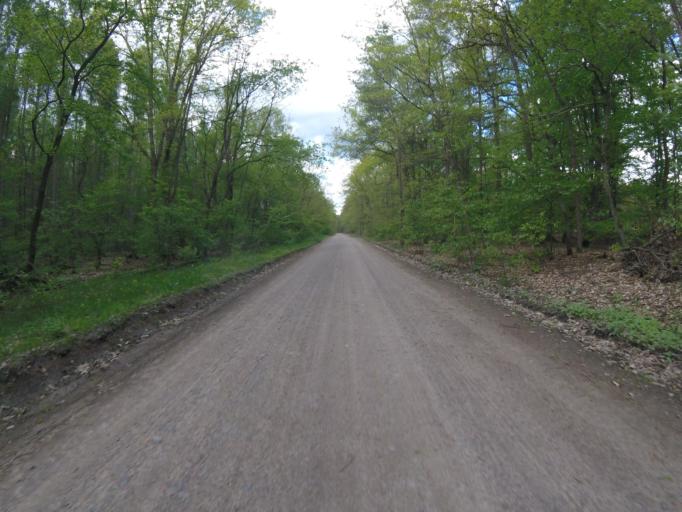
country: DE
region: Brandenburg
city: Schwerin
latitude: 52.1645
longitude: 13.5935
